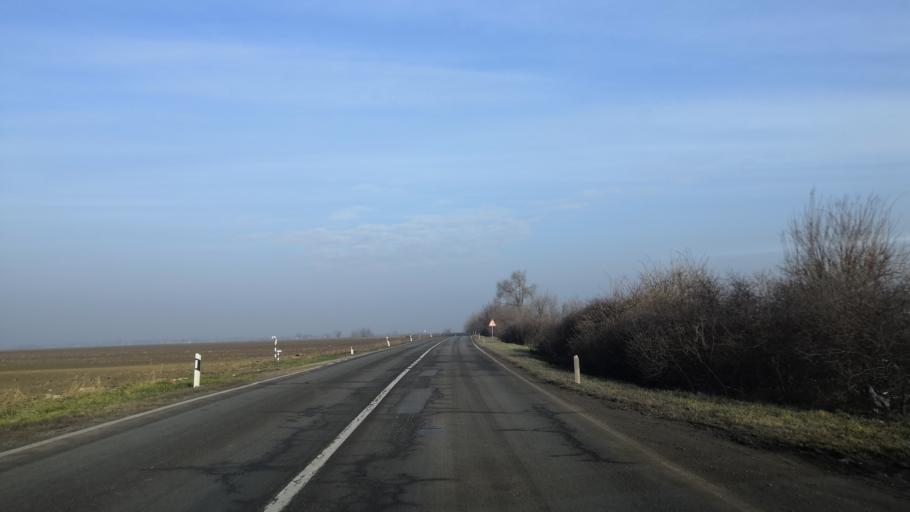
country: RS
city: Rumenka
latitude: 45.3215
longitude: 19.7373
